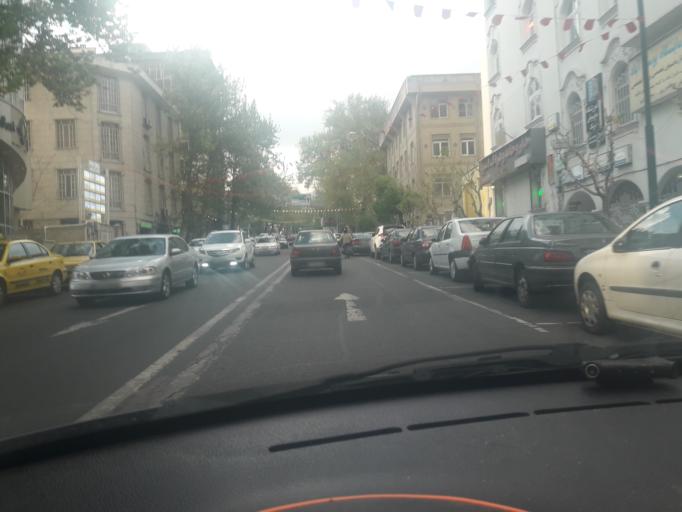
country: IR
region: Tehran
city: Tehran
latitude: 35.7431
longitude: 51.4051
